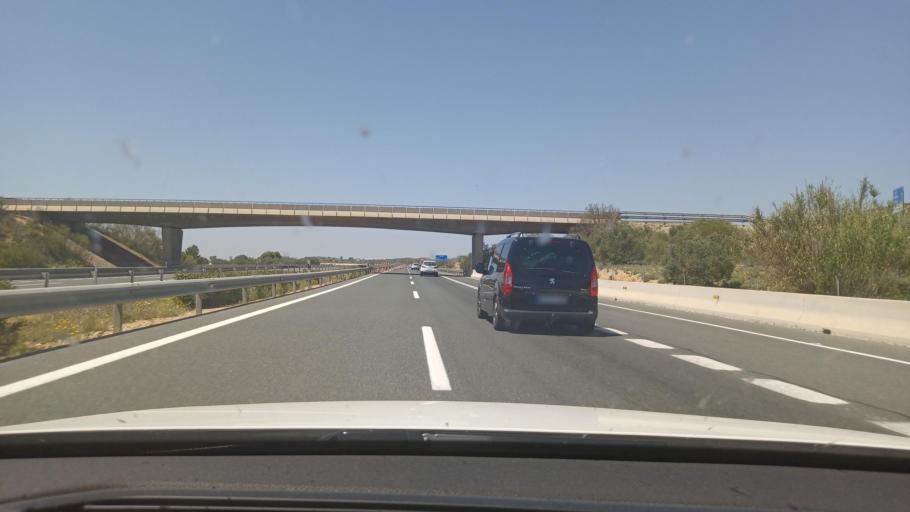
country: ES
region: Castille-La Mancha
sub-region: Provincia de Albacete
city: Almansa
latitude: 38.8771
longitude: -1.1726
